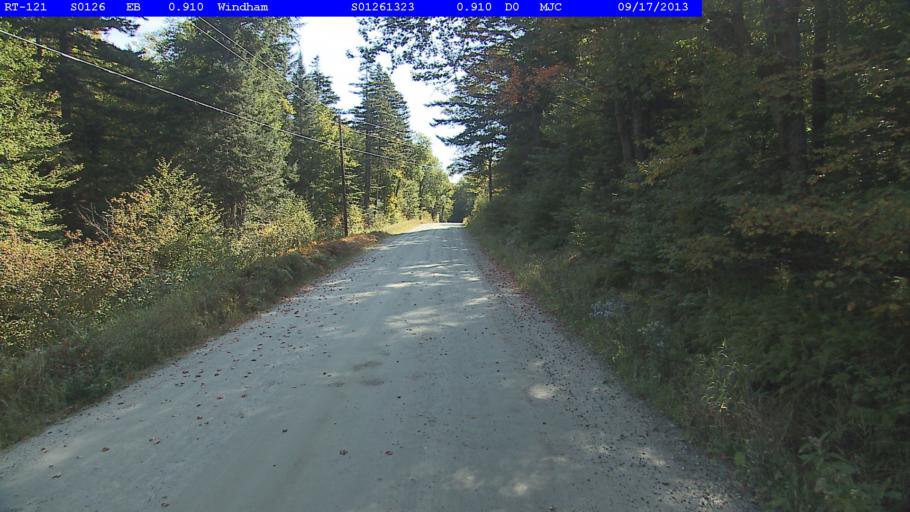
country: US
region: Vermont
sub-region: Windsor County
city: Chester
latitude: 43.1982
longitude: -72.7031
